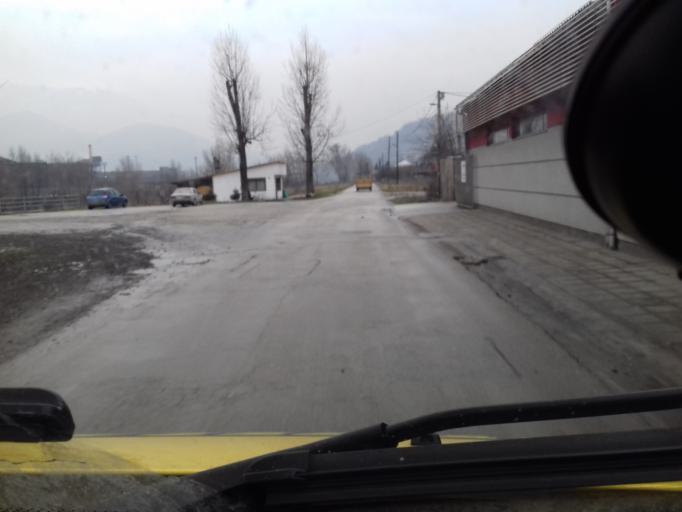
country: BA
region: Federation of Bosnia and Herzegovina
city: Zenica
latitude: 44.2217
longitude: 17.9088
